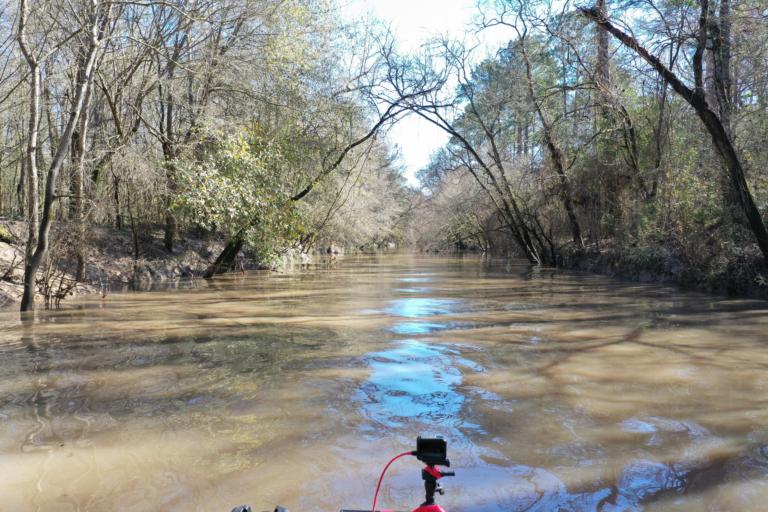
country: US
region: Louisiana
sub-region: Calcasieu Parish
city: Iowa
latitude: 30.3148
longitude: -93.0384
